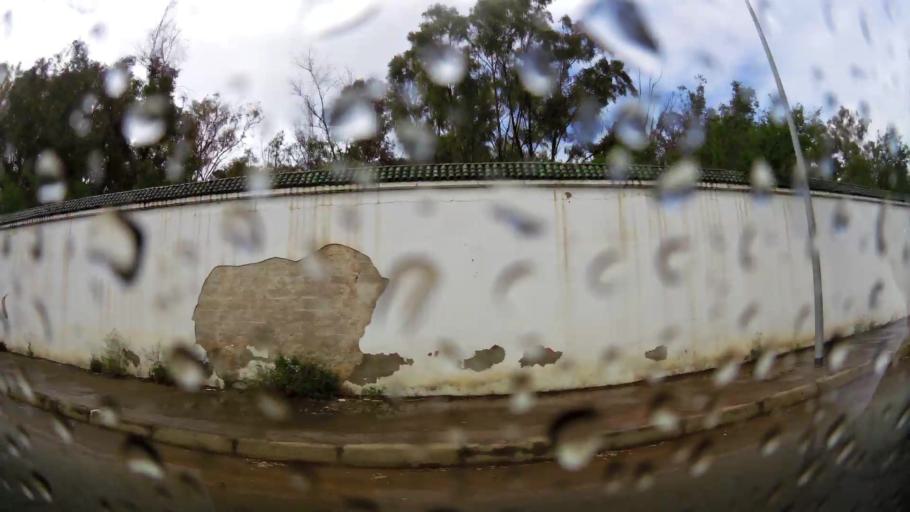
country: MA
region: Grand Casablanca
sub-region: Casablanca
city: Casablanca
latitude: 33.5275
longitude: -7.6274
